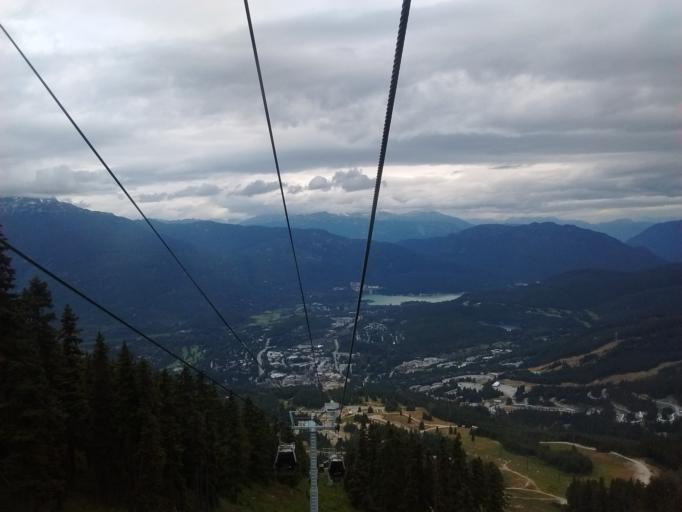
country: CA
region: British Columbia
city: Whistler
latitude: 50.0865
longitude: -122.9496
